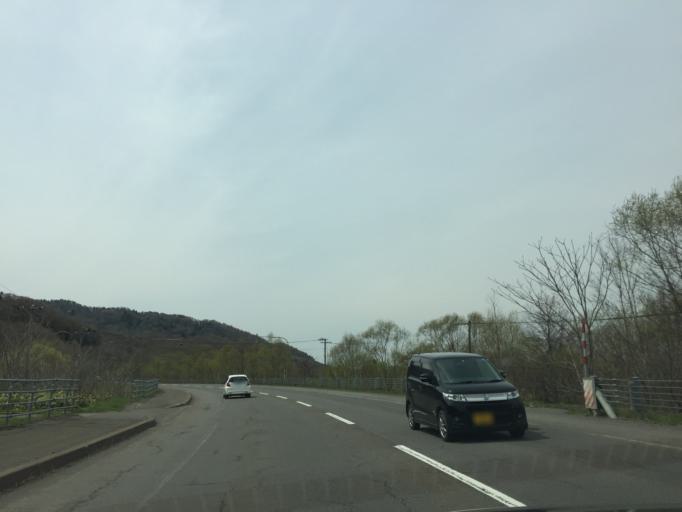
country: JP
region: Hokkaido
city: Ashibetsu
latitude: 43.5340
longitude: 142.1586
